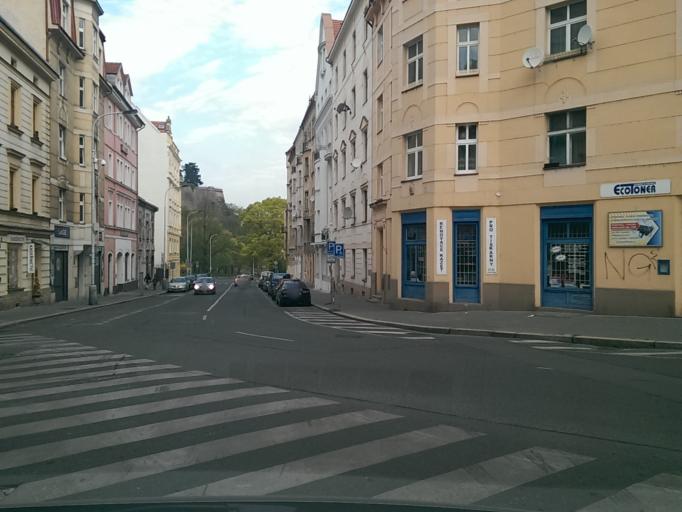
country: CZ
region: Praha
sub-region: Praha 2
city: Vysehrad
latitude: 50.0639
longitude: 14.4254
